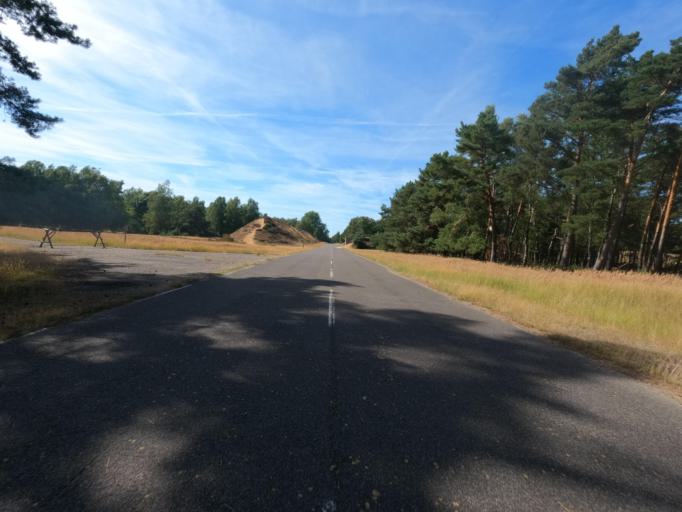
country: DE
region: North Rhine-Westphalia
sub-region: Regierungsbezirk Dusseldorf
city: Bruggen
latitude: 51.2618
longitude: 6.1539
